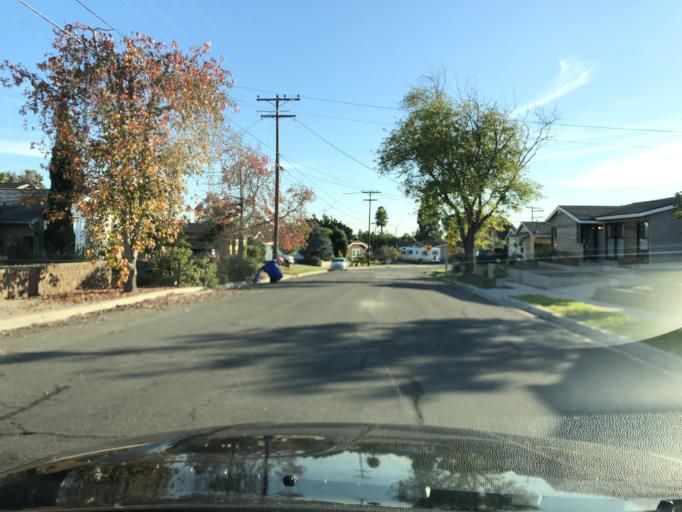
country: US
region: California
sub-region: San Diego County
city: La Jolla
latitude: 32.8195
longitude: -117.1853
